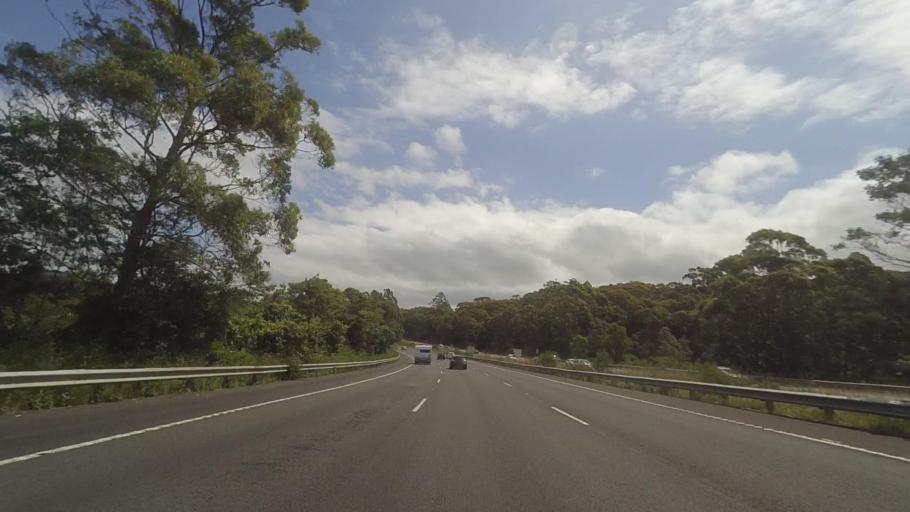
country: AU
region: New South Wales
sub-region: Gosford Shire
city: Lisarow
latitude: -33.3602
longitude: 151.3369
